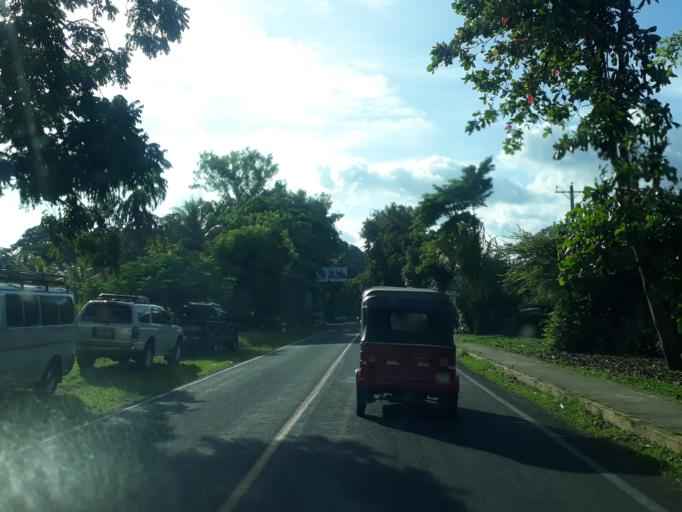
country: NI
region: Carazo
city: San Marcos
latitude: 11.9073
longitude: -86.1848
